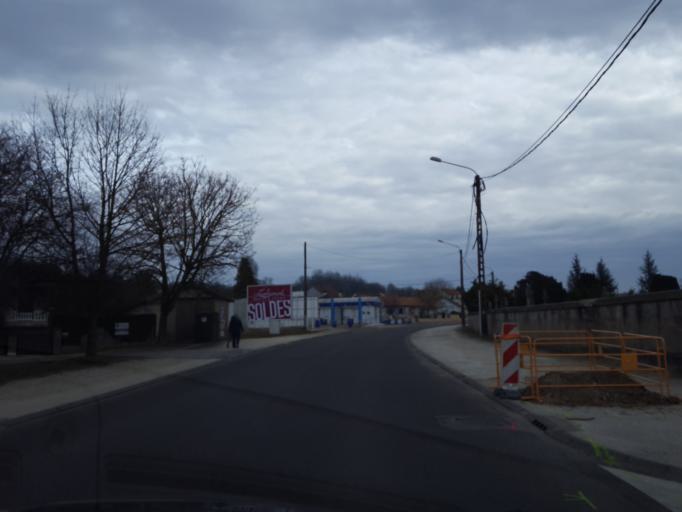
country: FR
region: Lorraine
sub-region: Departement de la Meuse
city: Verdun
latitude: 49.1674
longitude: 5.4018
